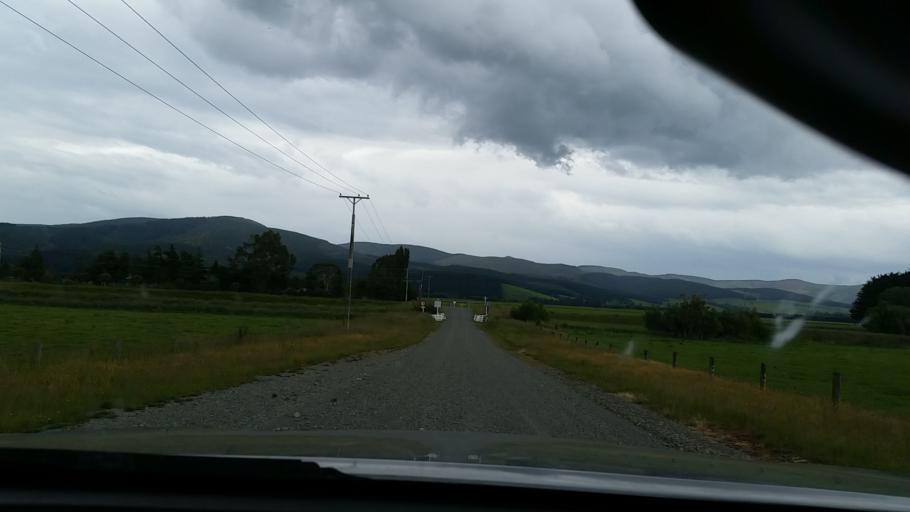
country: NZ
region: Southland
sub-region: Southland District
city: Winton
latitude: -45.9516
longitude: 168.3239
